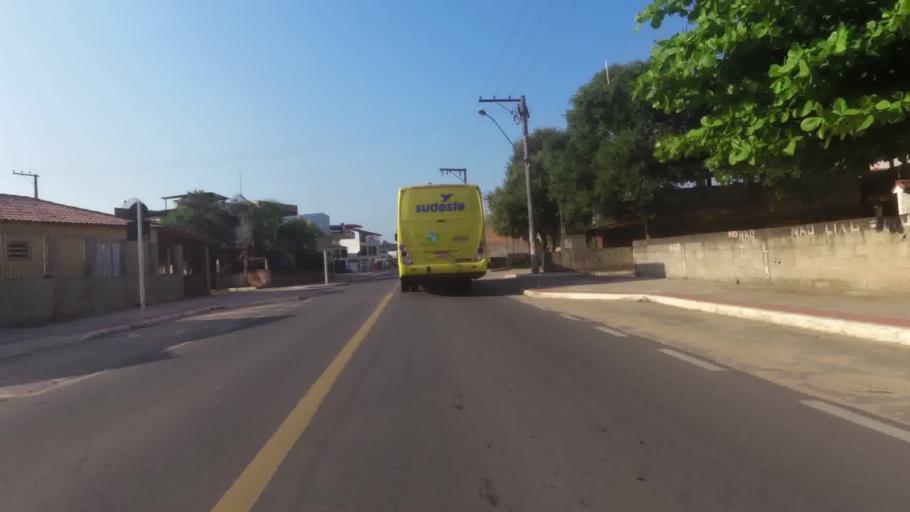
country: BR
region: Espirito Santo
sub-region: Piuma
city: Piuma
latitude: -20.8463
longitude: -40.7462
